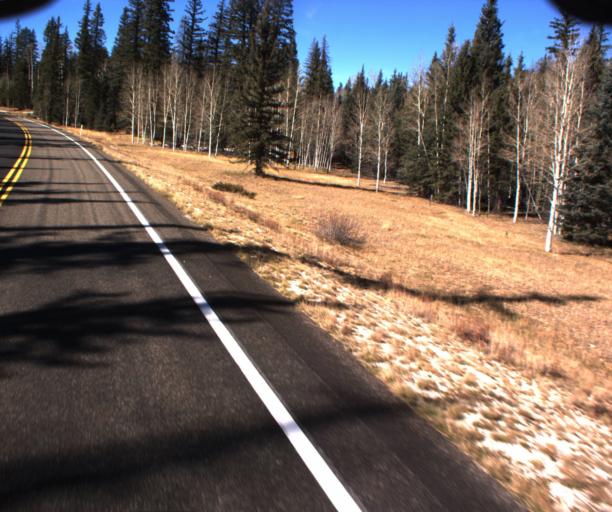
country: US
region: Arizona
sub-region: Coconino County
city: Grand Canyon
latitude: 36.5241
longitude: -112.1427
